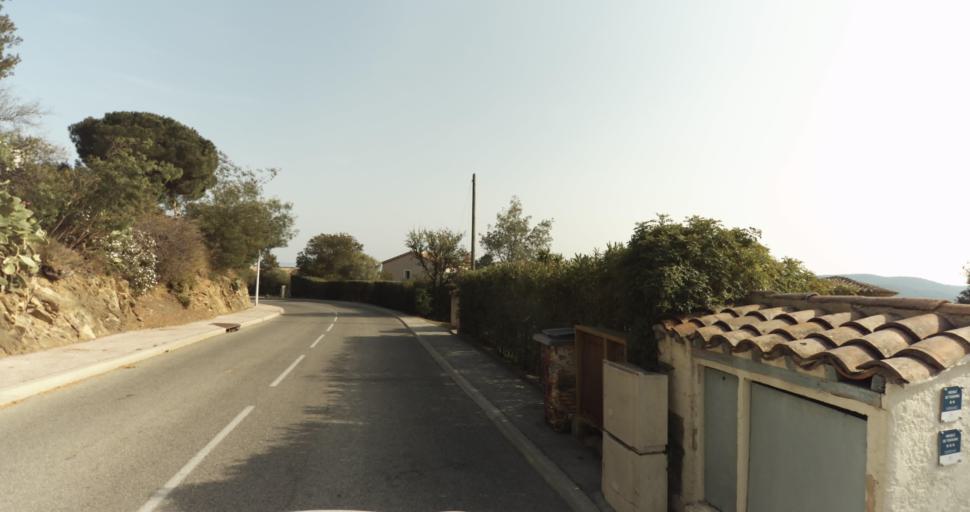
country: FR
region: Provence-Alpes-Cote d'Azur
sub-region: Departement du Var
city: Bormes-les-Mimosas
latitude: 43.1468
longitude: 6.3470
